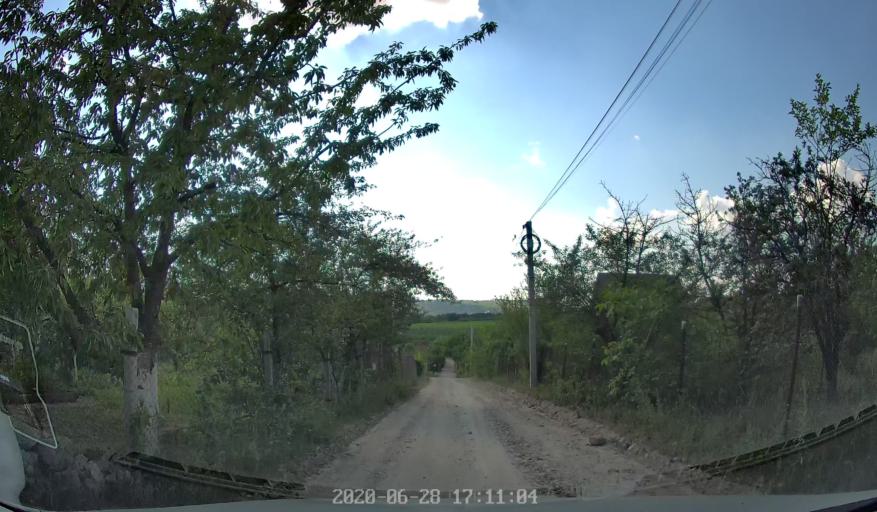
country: MD
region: Laloveni
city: Ialoveni
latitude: 46.9867
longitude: 28.6996
